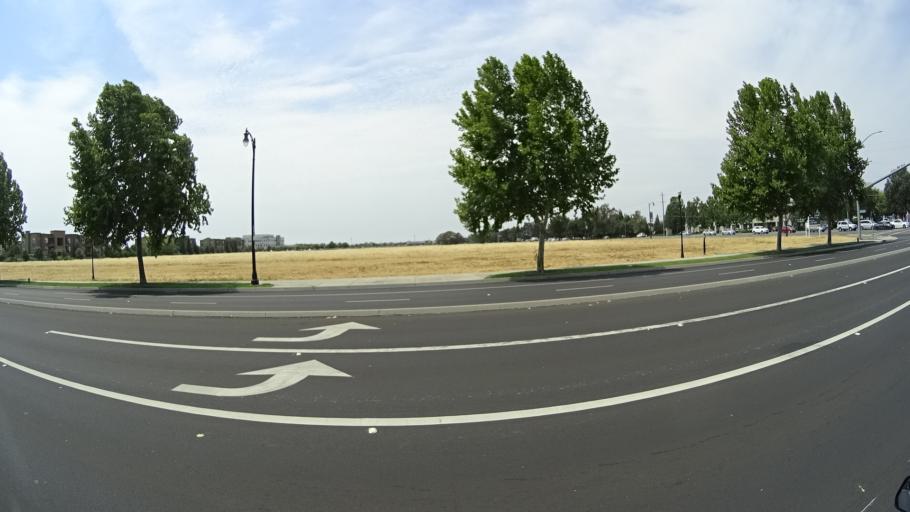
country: US
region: California
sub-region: Sacramento County
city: Laguna
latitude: 38.4084
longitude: -121.4051
